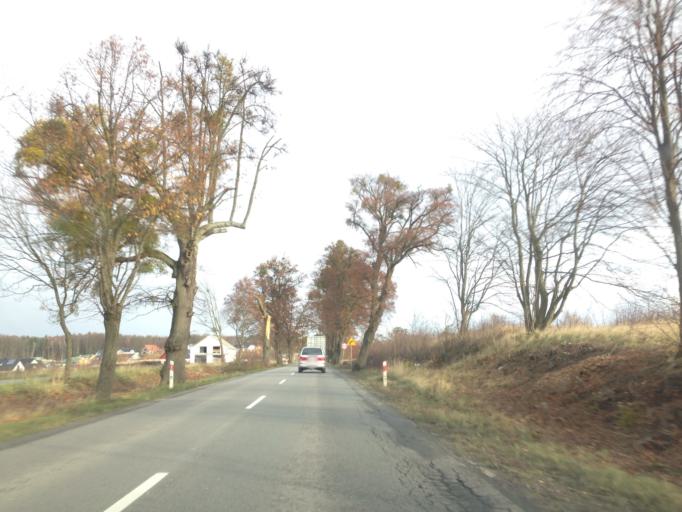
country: PL
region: Pomeranian Voivodeship
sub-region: Powiat gdanski
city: Kowale
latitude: 54.2984
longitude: 18.5364
